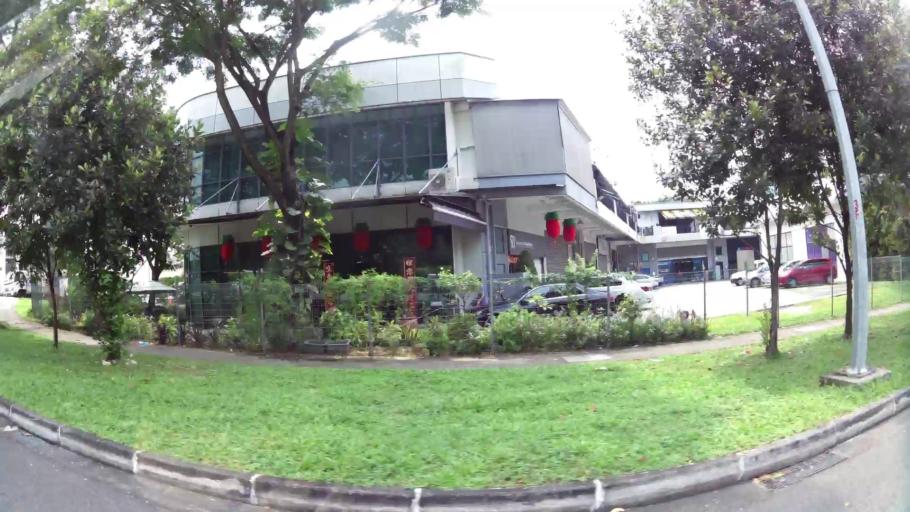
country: SG
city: Singapore
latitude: 1.3383
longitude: 103.9034
